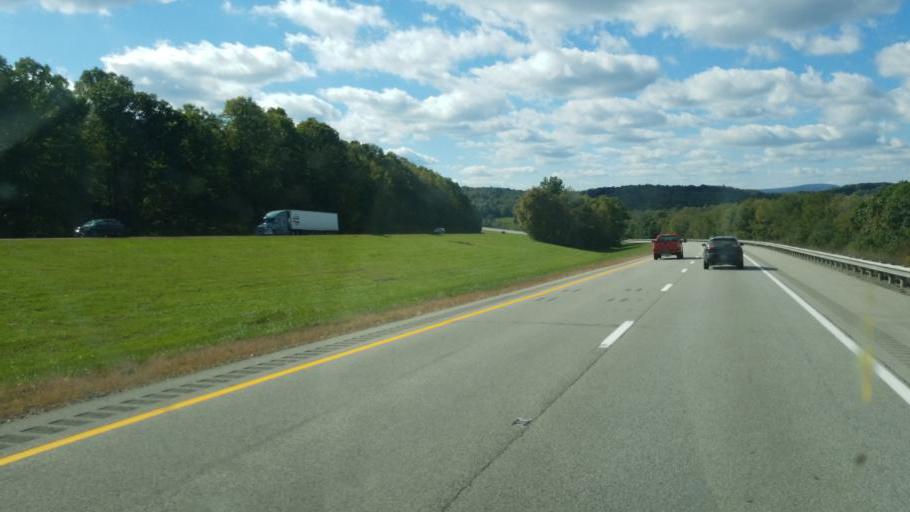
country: US
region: West Virginia
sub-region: Preston County
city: Kingwood
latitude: 39.6625
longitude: -79.5867
